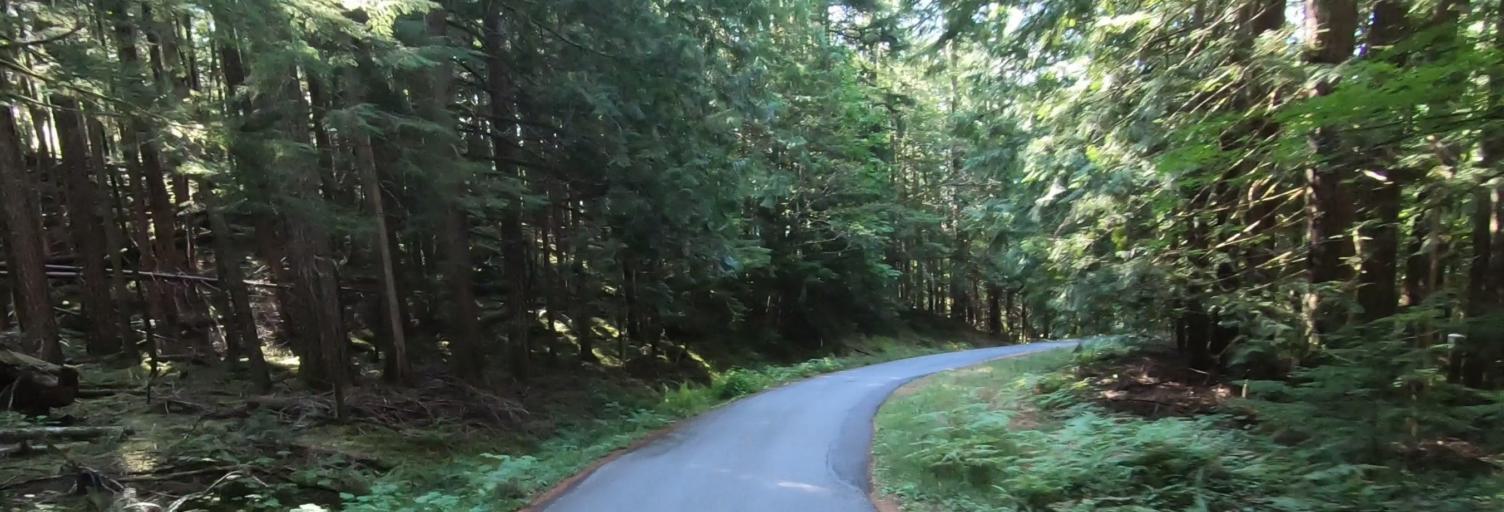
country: US
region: Washington
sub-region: Whatcom County
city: Peaceful Valley
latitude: 48.9027
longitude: -121.9290
